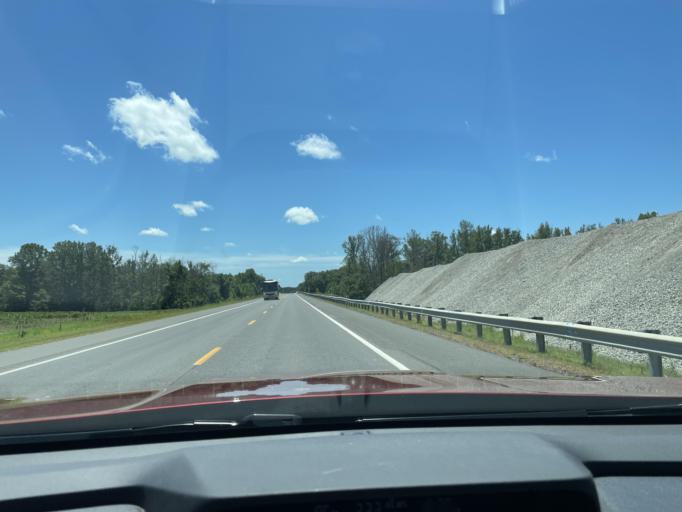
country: US
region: Arkansas
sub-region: Jefferson County
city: Pine Bluff
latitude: 34.1459
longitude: -91.9770
